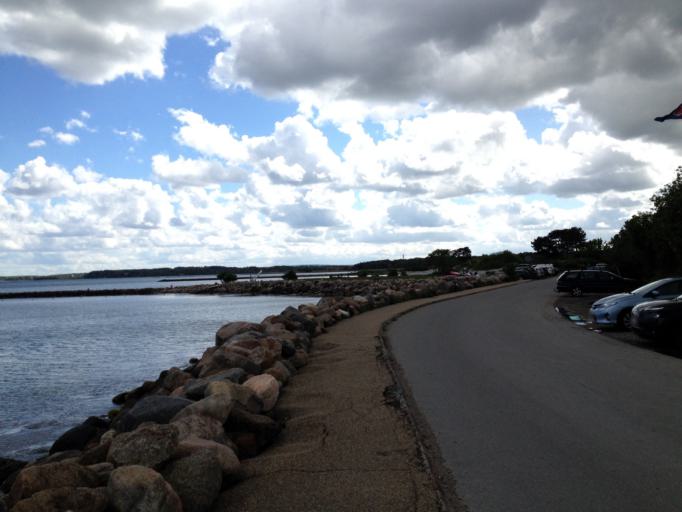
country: DK
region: Capital Region
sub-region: Fredensborg Kommune
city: Humlebaek
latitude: 55.9389
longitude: 12.5292
